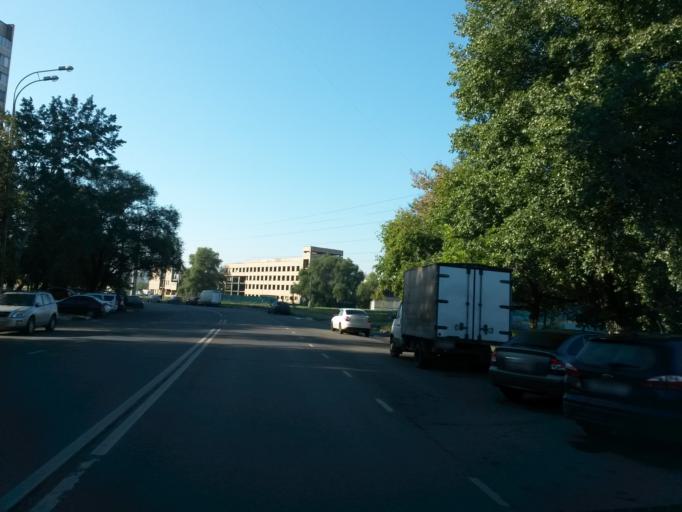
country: RU
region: Moscow
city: Mar'ino
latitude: 55.6508
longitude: 37.7084
